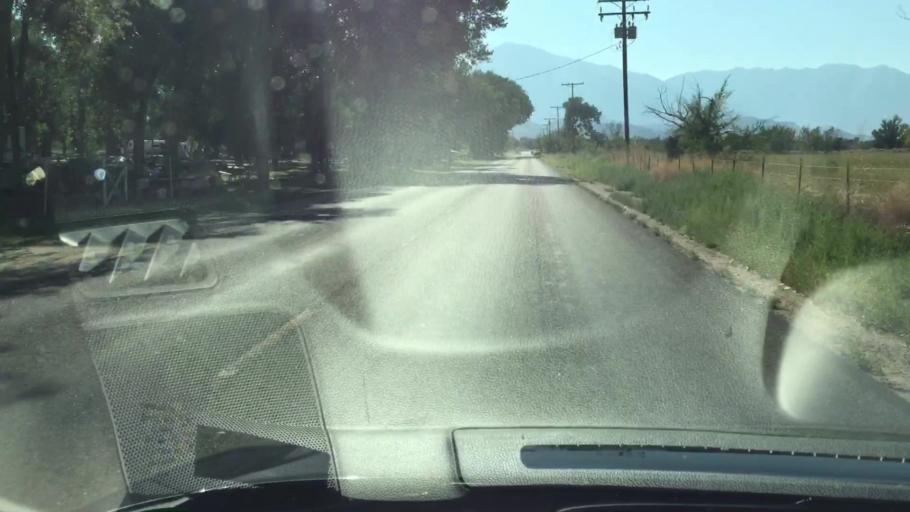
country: US
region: California
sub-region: Inyo County
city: Bishop
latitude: 37.3469
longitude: -118.3967
